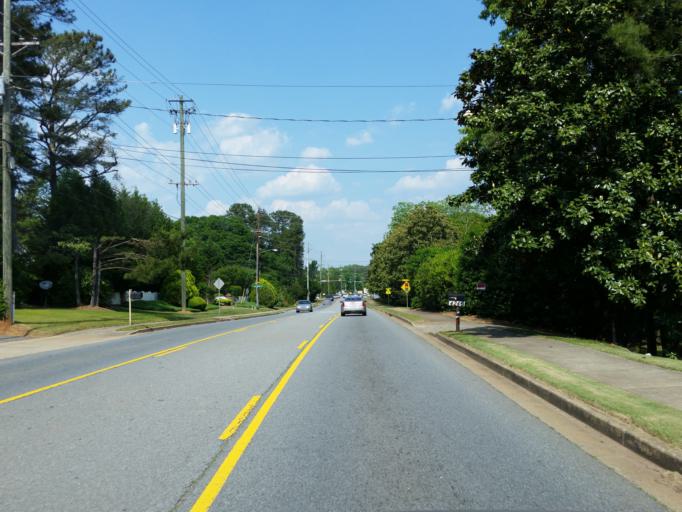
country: US
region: Georgia
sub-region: Fulton County
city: Sandy Springs
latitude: 33.9623
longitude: -84.4278
